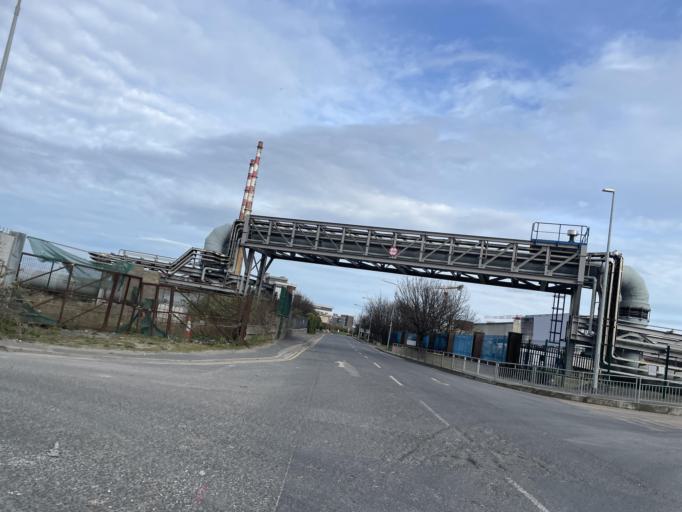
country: IE
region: Leinster
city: Sandymount
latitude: 53.3405
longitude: -6.1991
